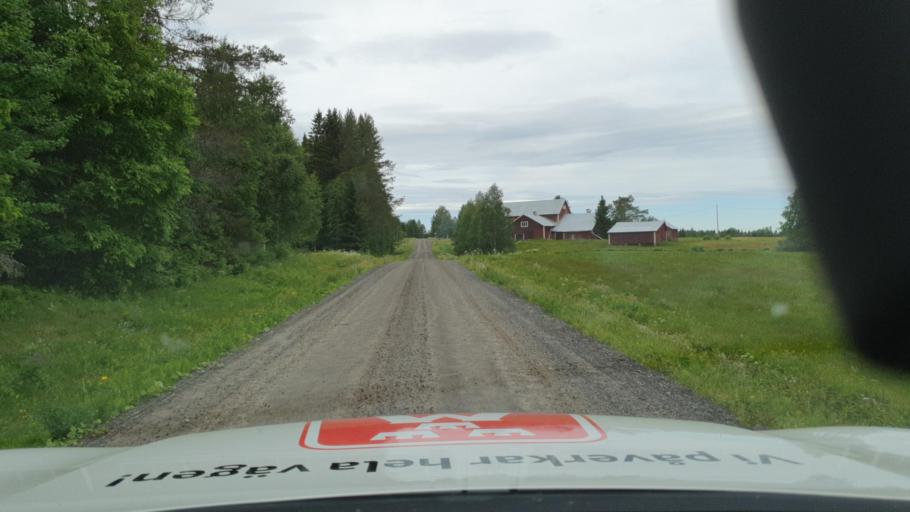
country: SE
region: Vaesterbotten
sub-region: Skelleftea Kommun
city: Burtraesk
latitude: 64.3917
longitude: 20.6021
